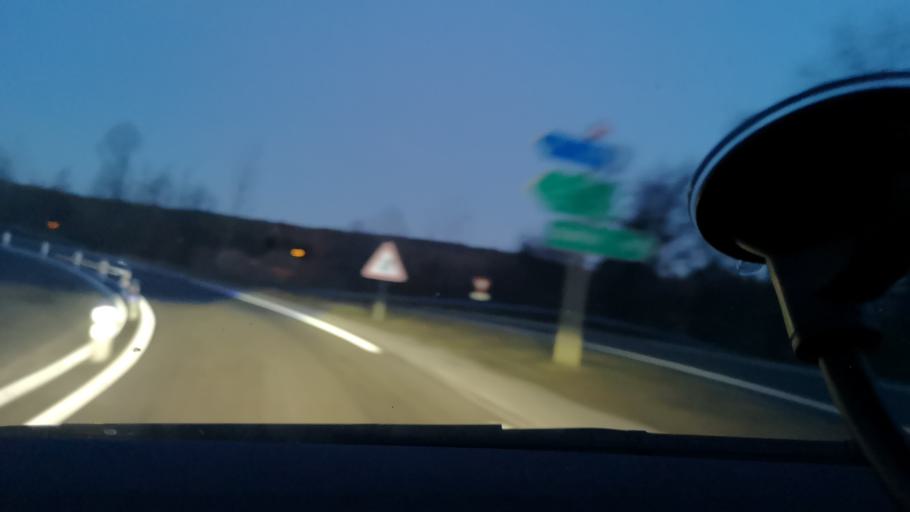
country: FR
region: Franche-Comte
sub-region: Departement du Jura
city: Champagnole
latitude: 46.7451
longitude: 5.9243
